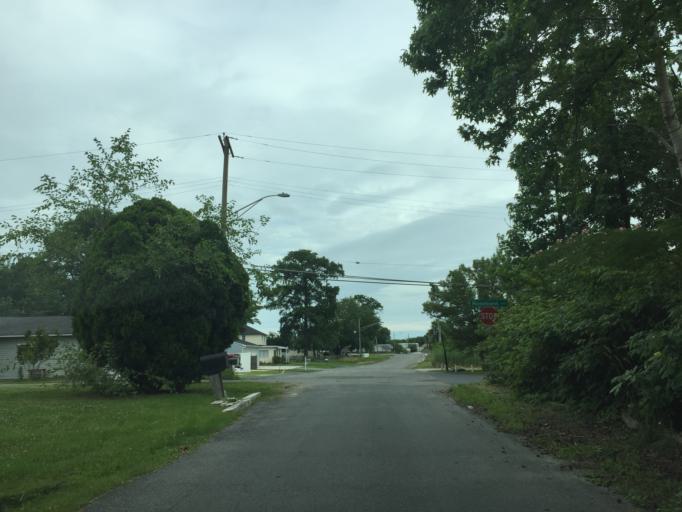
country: US
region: Maryland
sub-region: Baltimore County
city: Essex
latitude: 39.2830
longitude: -76.4717
